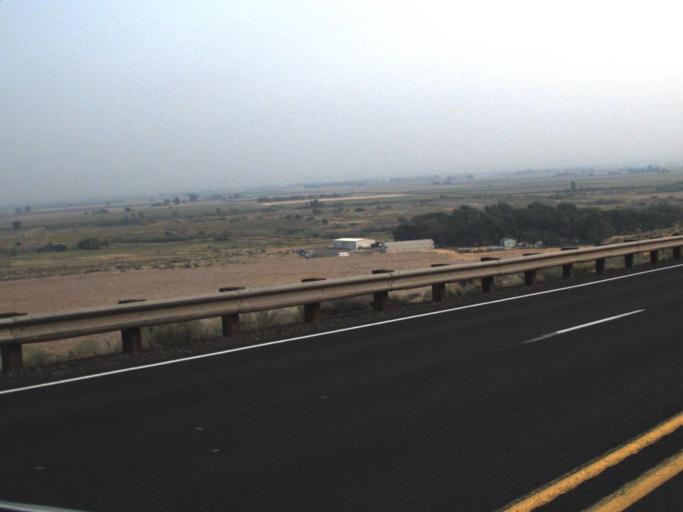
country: US
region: Washington
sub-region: Yakima County
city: Toppenish
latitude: 46.3003
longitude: -120.3490
